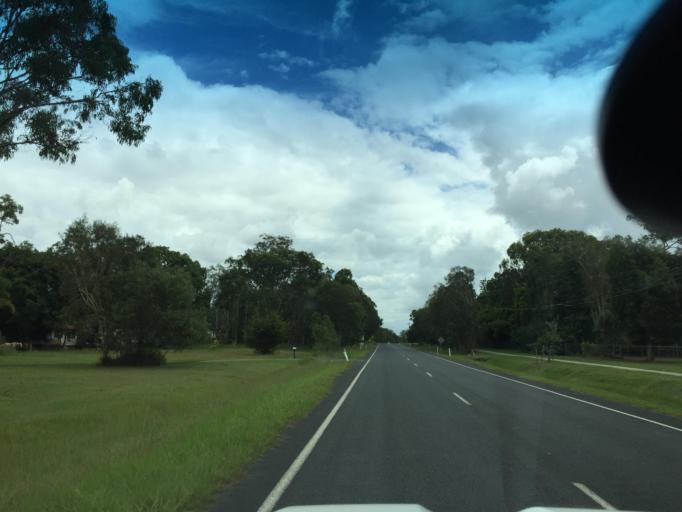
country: AU
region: Queensland
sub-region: Moreton Bay
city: Caboolture
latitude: -27.0474
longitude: 152.9359
